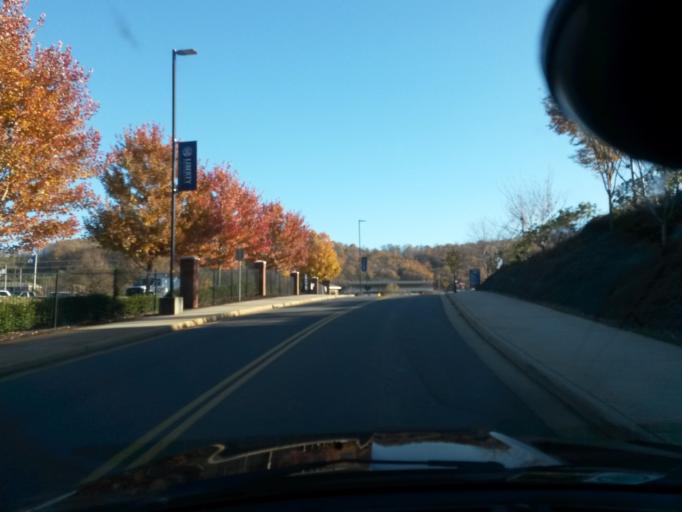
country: US
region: Virginia
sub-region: City of Lynchburg
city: West Lynchburg
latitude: 37.3537
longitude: -79.1769
